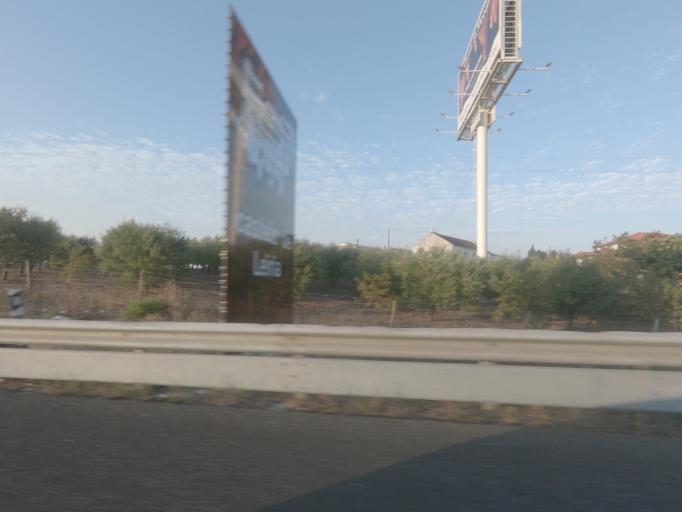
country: PT
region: Leiria
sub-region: Leiria
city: Santa Catarina da Serra
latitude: 39.7009
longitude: -8.6979
